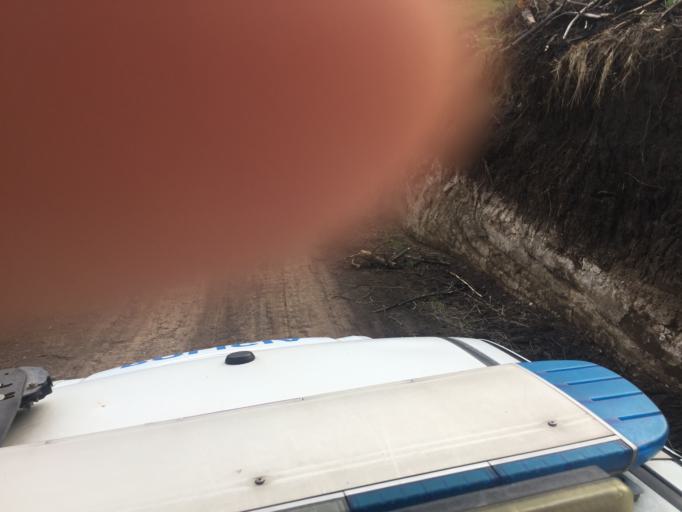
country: EC
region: Imbabura
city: Ibarra
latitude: 0.2275
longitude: -78.1207
